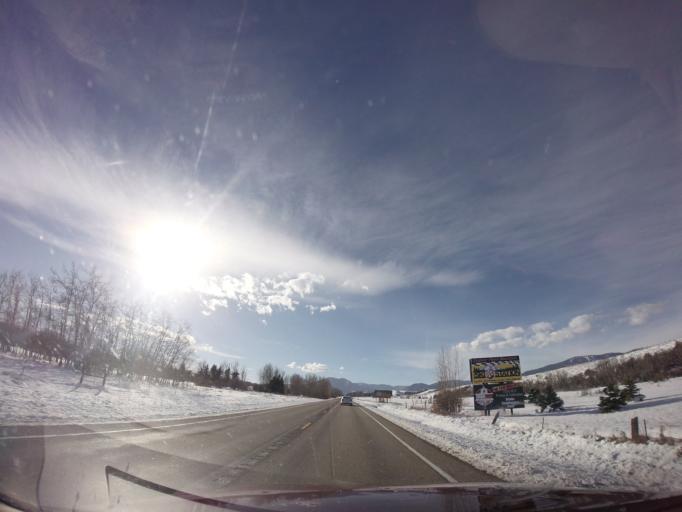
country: US
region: Montana
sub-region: Carbon County
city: Red Lodge
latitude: 45.2471
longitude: -109.2345
